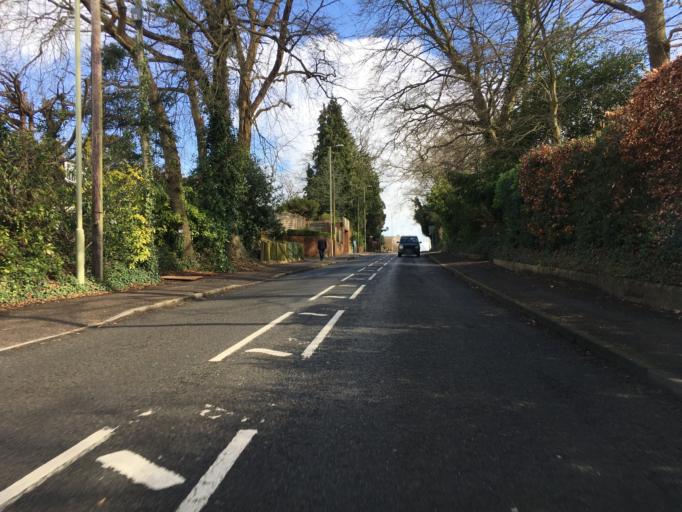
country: GB
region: England
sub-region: Hampshire
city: Chandlers Ford
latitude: 50.9862
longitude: -1.3787
